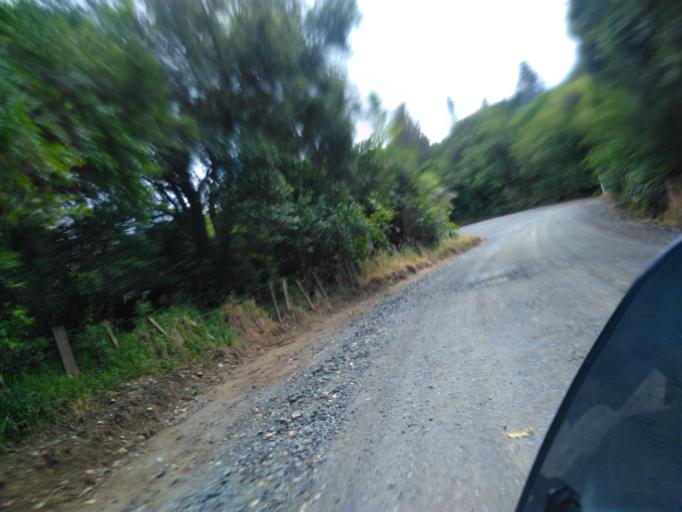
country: NZ
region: Gisborne
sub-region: Gisborne District
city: Gisborne
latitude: -38.2372
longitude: 178.0697
